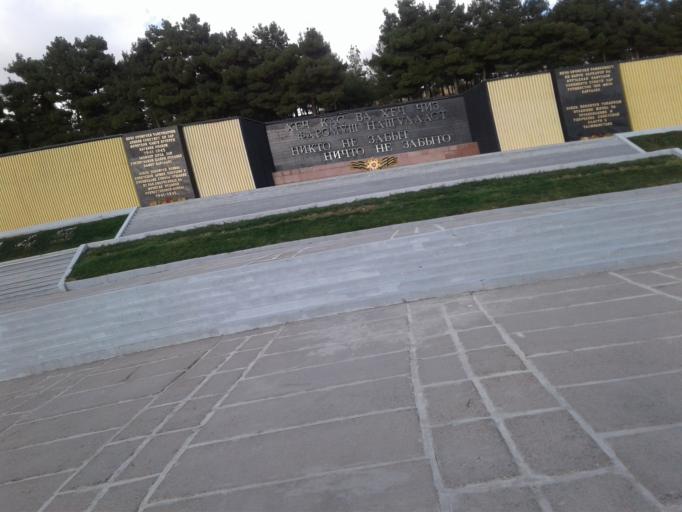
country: TJ
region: Dushanbe
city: Dushanbe
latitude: 38.5814
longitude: 68.8138
